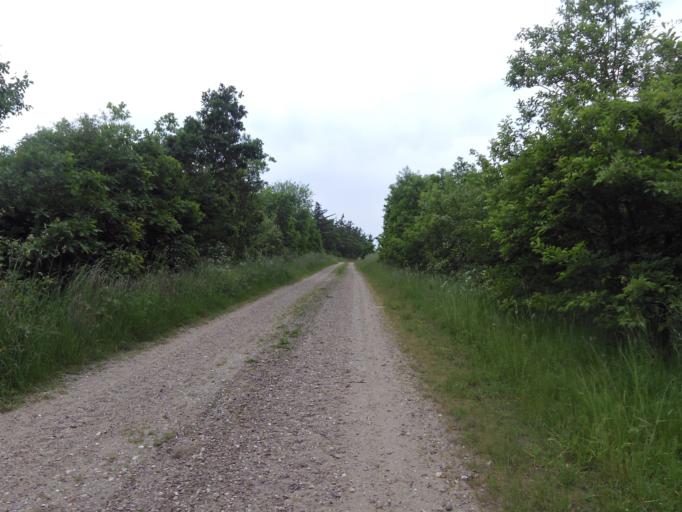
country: DK
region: South Denmark
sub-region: Esbjerg Kommune
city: Ribe
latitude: 55.3207
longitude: 8.8411
